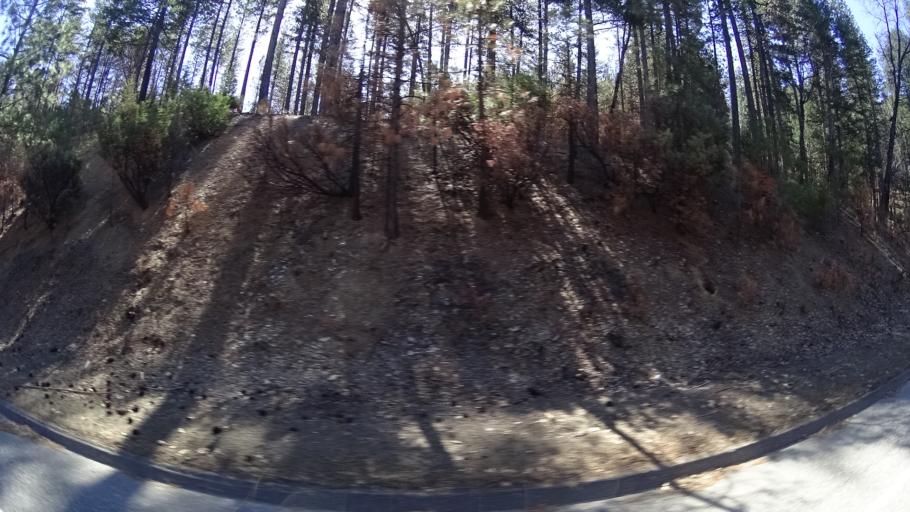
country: US
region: California
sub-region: Tehama County
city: Rancho Tehama Reserve
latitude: 39.6574
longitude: -122.7247
